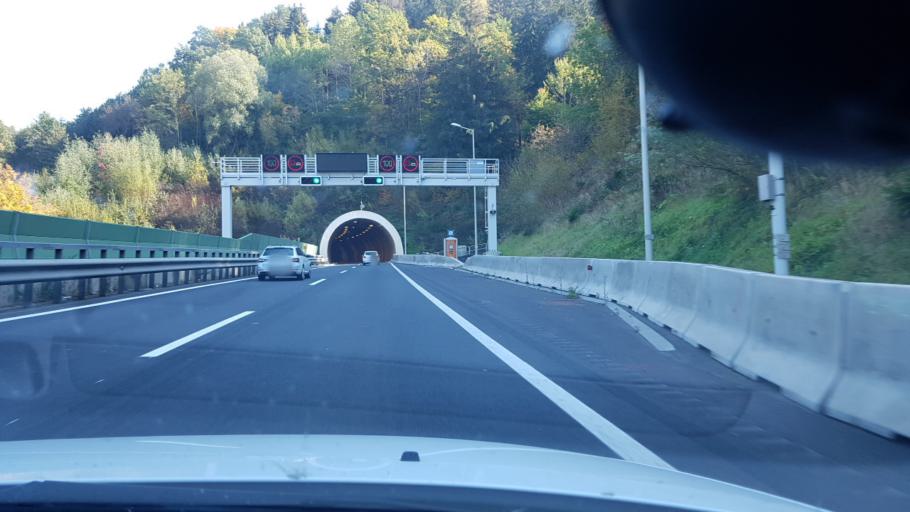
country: AT
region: Styria
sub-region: Politischer Bezirk Bruck-Muerzzuschlag
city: Oberaich
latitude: 47.3989
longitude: 15.2444
